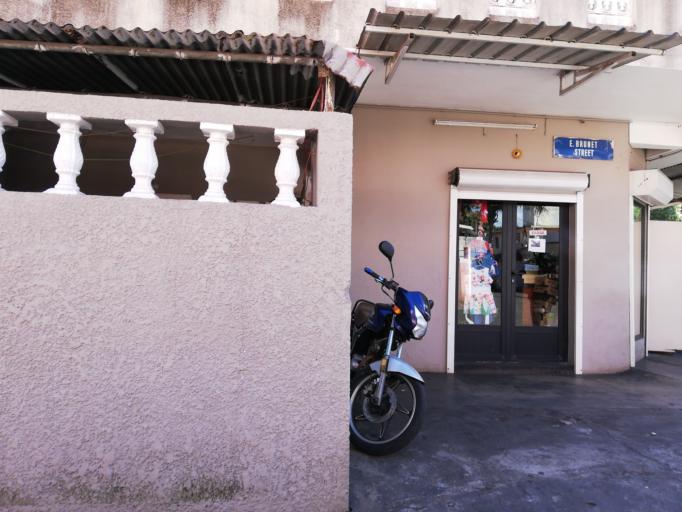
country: MU
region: Moka
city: Moka
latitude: -20.2173
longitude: 57.4672
